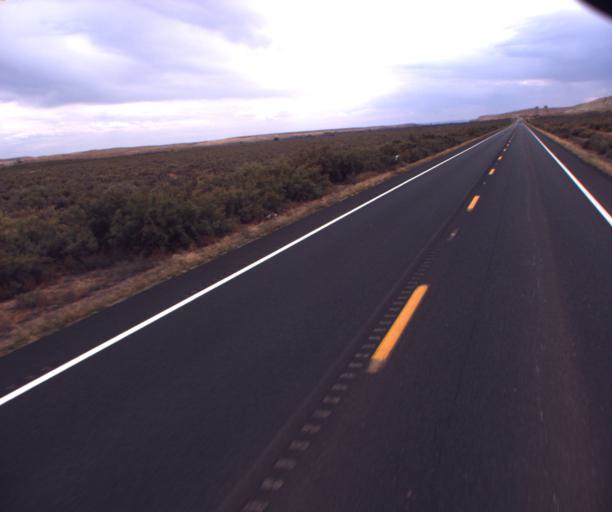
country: US
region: Arizona
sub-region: Coconino County
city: Kaibito
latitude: 36.3410
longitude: -110.9172
